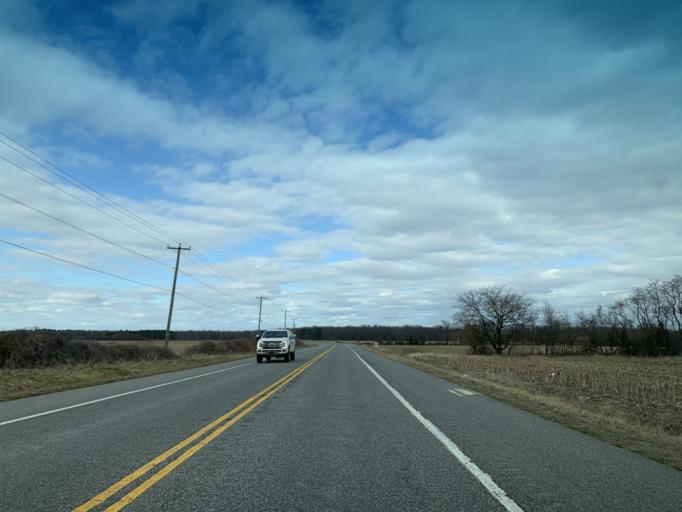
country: US
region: Maryland
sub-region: Queen Anne's County
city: Centreville
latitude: 38.9697
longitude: -76.0744
